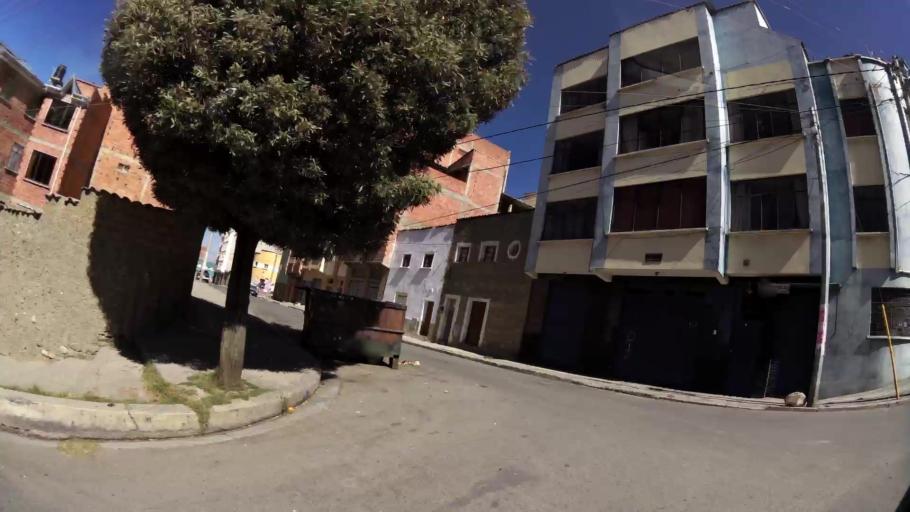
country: BO
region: La Paz
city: La Paz
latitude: -16.4918
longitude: -68.1608
